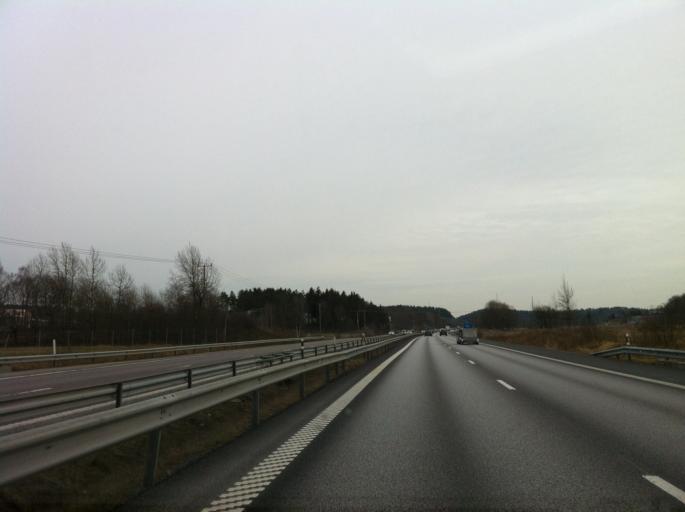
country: SE
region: Vaestra Goetaland
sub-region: Kungalvs Kommun
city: Kode
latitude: 57.9308
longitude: 11.8730
